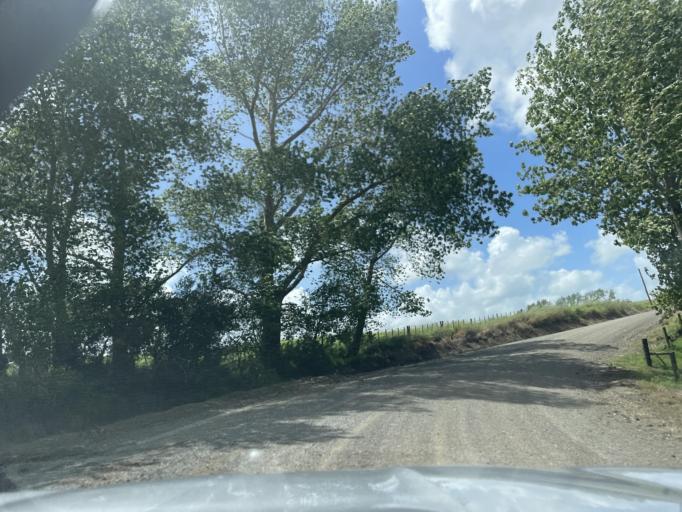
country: NZ
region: Auckland
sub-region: Auckland
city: Wellsford
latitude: -36.1732
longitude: 174.3171
